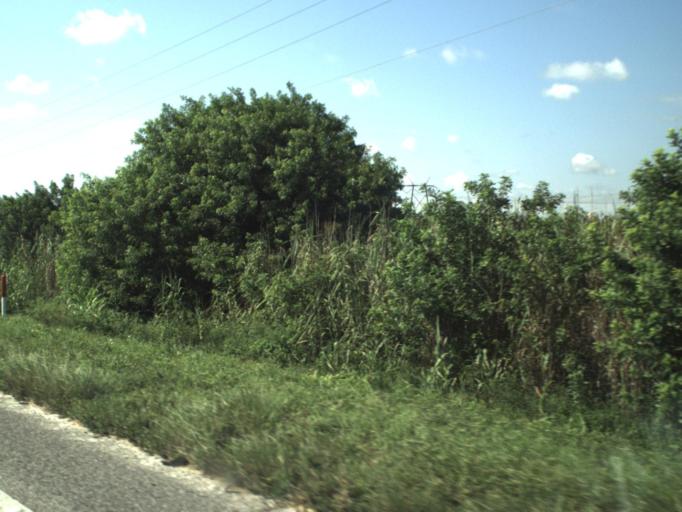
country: US
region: Florida
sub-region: Broward County
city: Weston
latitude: 26.3308
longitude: -80.5349
